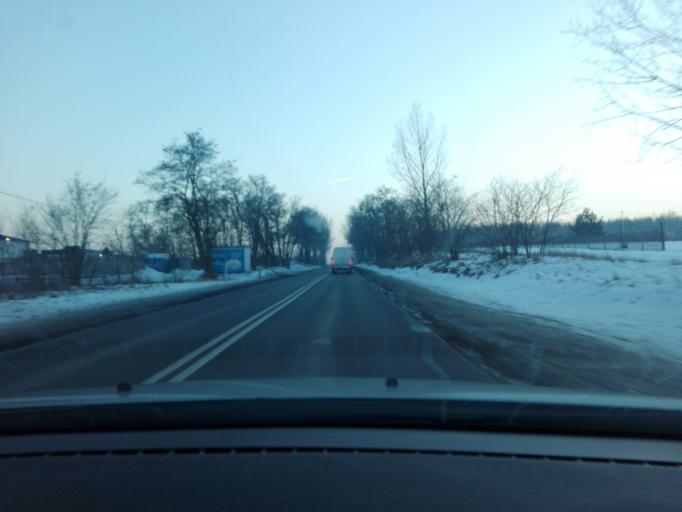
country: PL
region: Lodz Voivodeship
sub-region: Powiat zgierski
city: Zgierz
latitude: 51.8906
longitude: 19.4194
